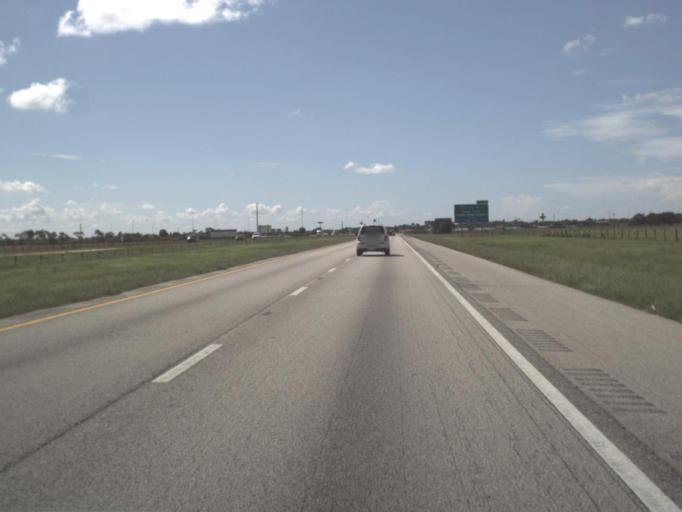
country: US
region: Florida
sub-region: Charlotte County
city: Punta Gorda
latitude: 26.9082
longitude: -82.0099
